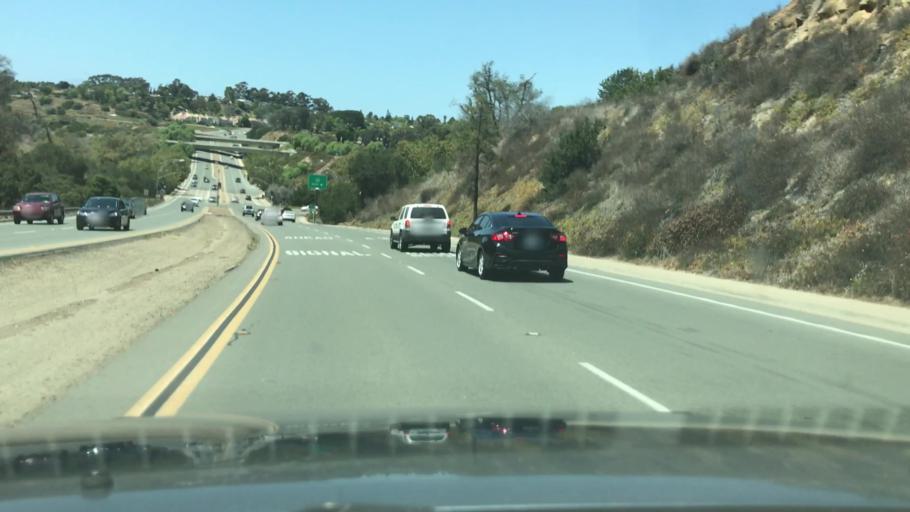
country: US
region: California
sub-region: San Diego County
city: La Jolla
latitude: 32.8434
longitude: -117.1982
